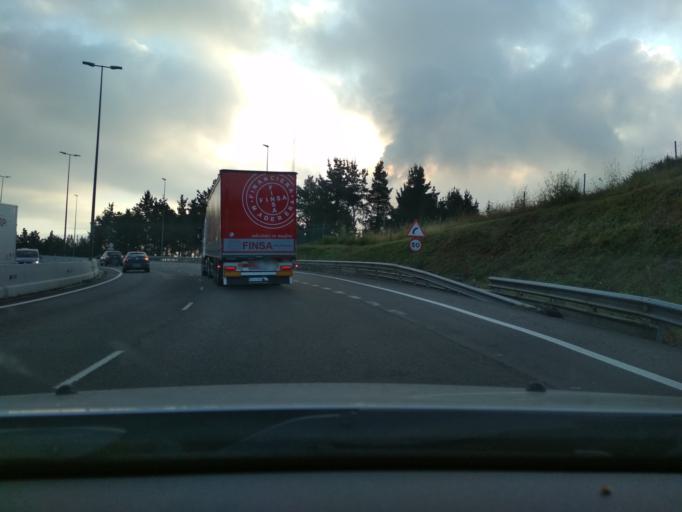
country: ES
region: Galicia
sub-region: Provincia da Coruna
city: Santiago de Compostela
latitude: 42.9061
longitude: -8.5098
